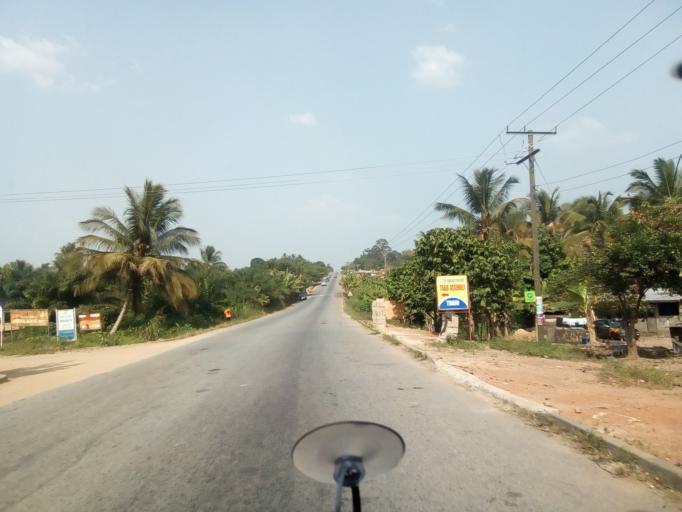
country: GH
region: Eastern
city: Suhum
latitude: 6.0643
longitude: -0.3998
